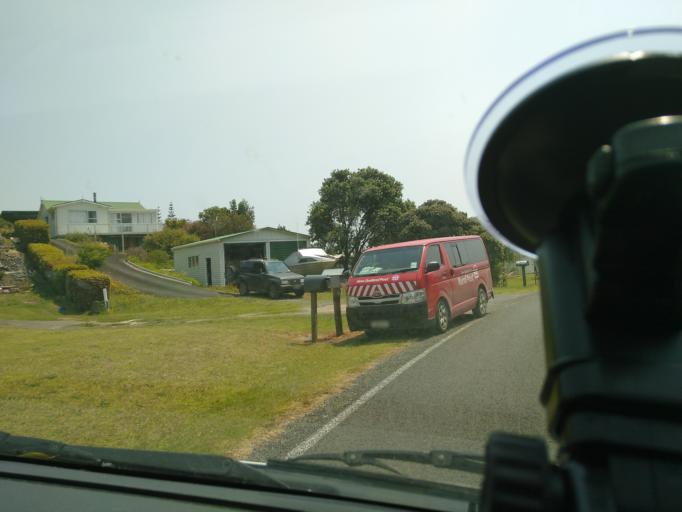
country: NZ
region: Northland
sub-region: Far North District
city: Kaitaia
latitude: -34.8159
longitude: 173.1165
